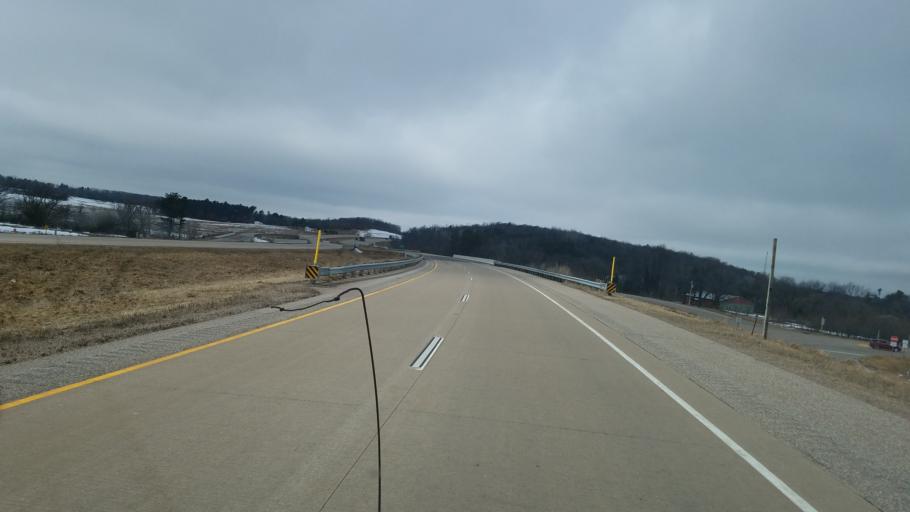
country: US
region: Wisconsin
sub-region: Portage County
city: Amherst
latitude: 44.4376
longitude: -89.2814
